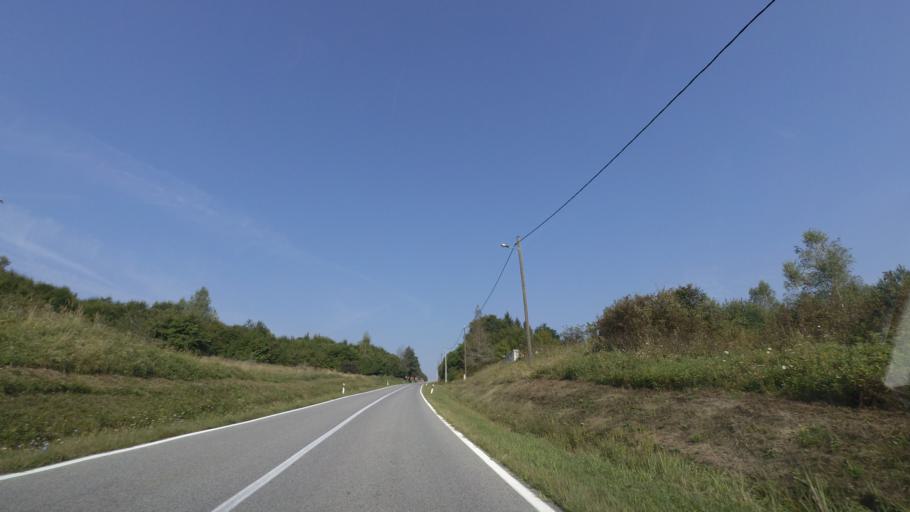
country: HR
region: Bjelovarsko-Bilogorska
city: Sirac
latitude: 45.4634
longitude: 17.4067
